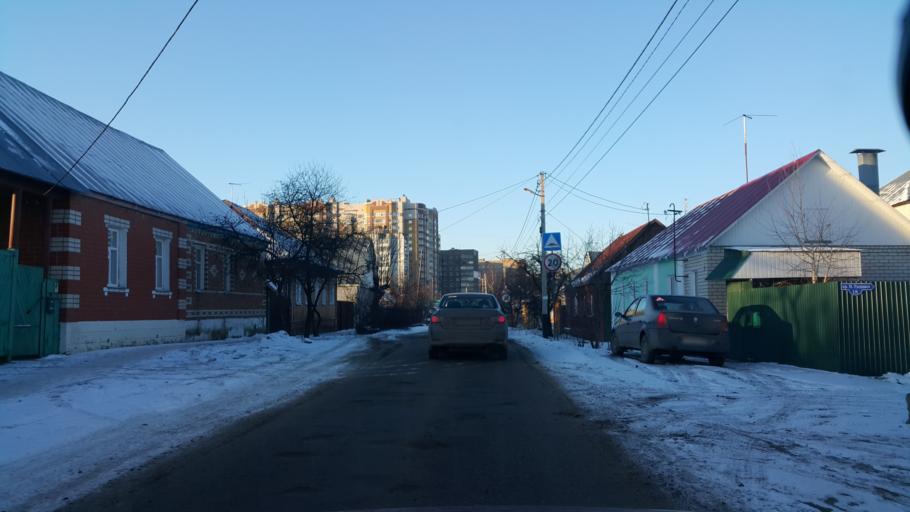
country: RU
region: Tambov
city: Pokrovo-Prigorodnoye
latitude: 52.7021
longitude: 41.4009
